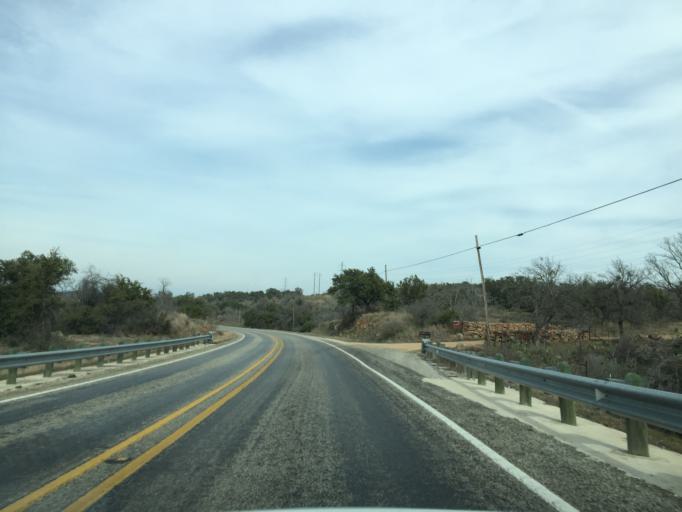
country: US
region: Texas
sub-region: Gillespie County
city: Fredericksburg
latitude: 30.4681
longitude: -98.7165
